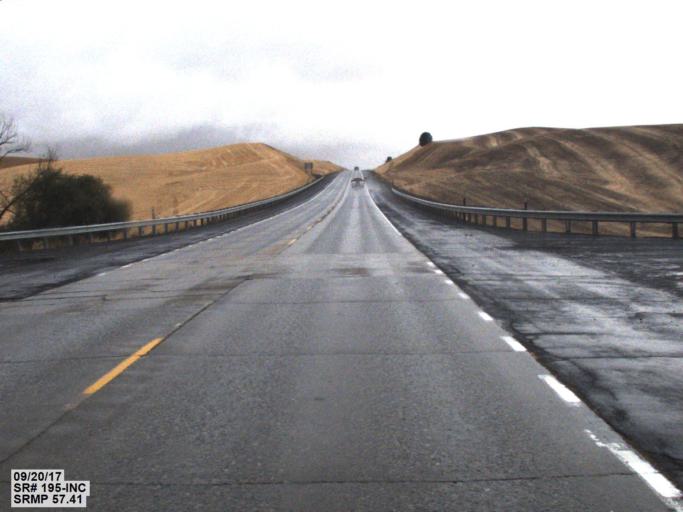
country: US
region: Washington
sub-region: Whitman County
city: Colfax
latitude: 47.1374
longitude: -117.3794
